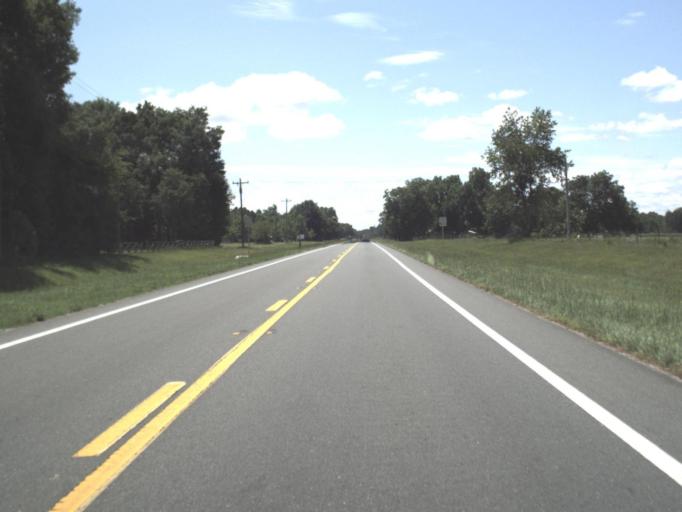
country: US
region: Florida
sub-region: Lafayette County
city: Mayo
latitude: 30.1104
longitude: -83.2522
